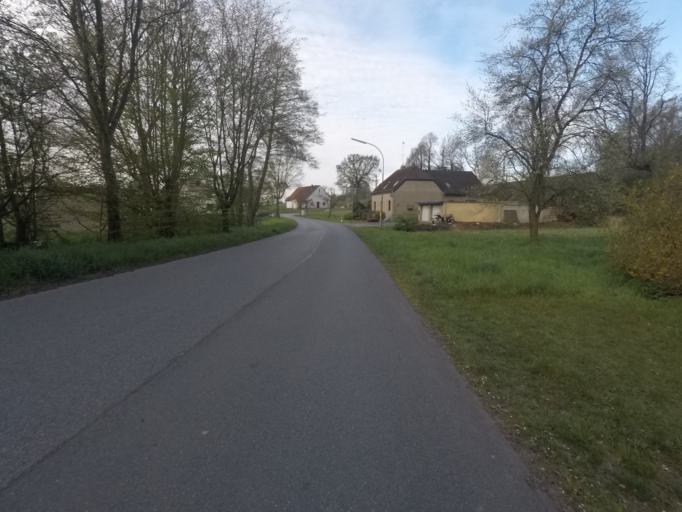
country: DE
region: North Rhine-Westphalia
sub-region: Regierungsbezirk Detmold
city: Herford
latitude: 52.0857
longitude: 8.6218
